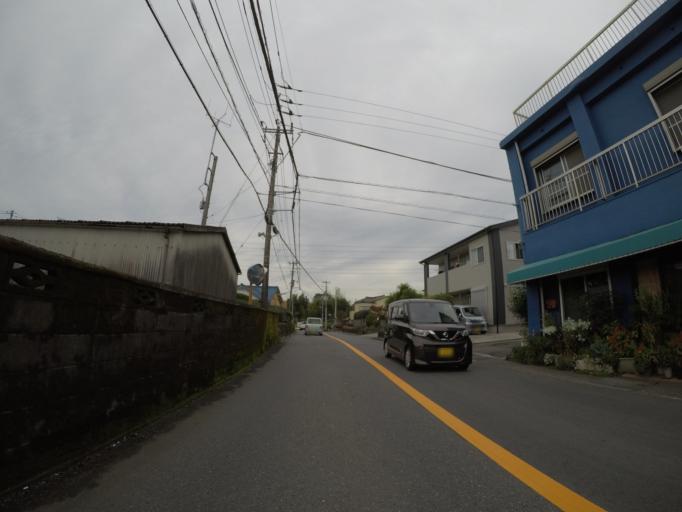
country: JP
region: Shizuoka
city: Fuji
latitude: 35.1888
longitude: 138.7011
